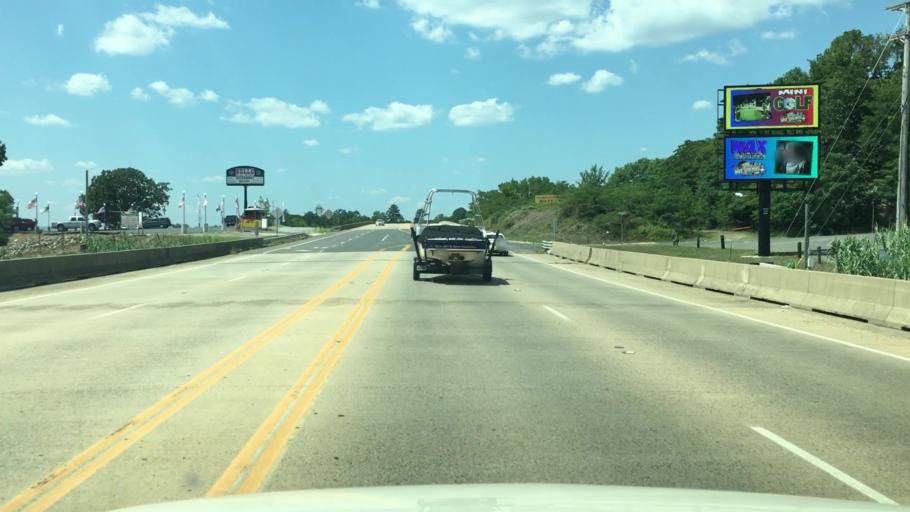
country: US
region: Arkansas
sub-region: Garland County
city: Lake Hamilton
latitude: 34.4304
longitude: -93.0854
